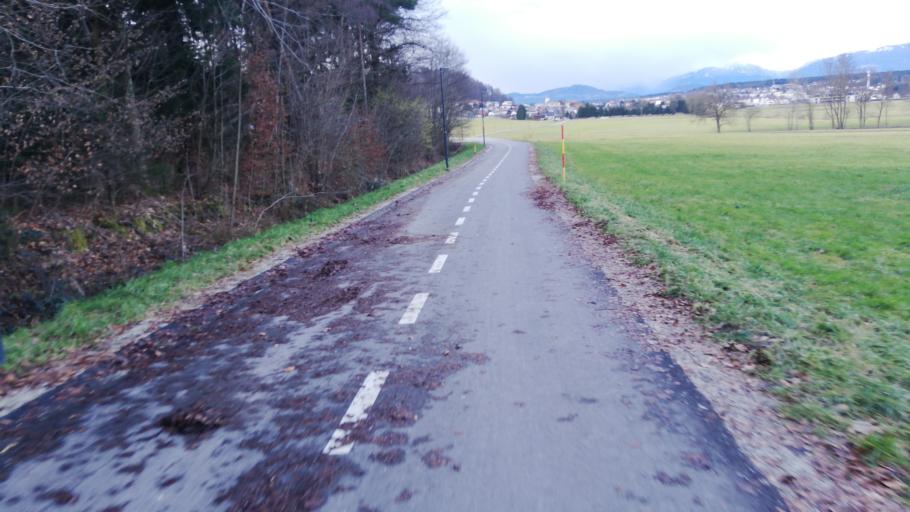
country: SI
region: Medvode
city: Medvode
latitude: 46.1239
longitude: 14.4200
